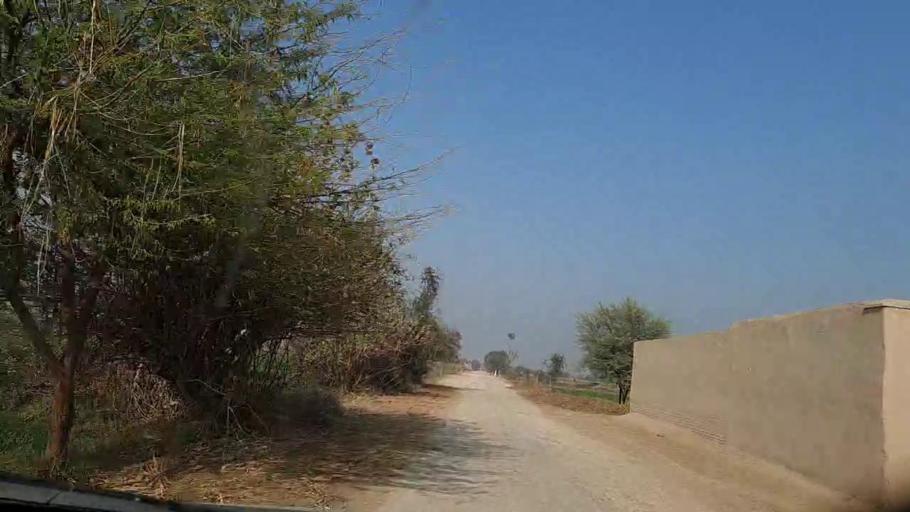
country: PK
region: Sindh
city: Moro
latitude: 26.7789
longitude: 67.9352
